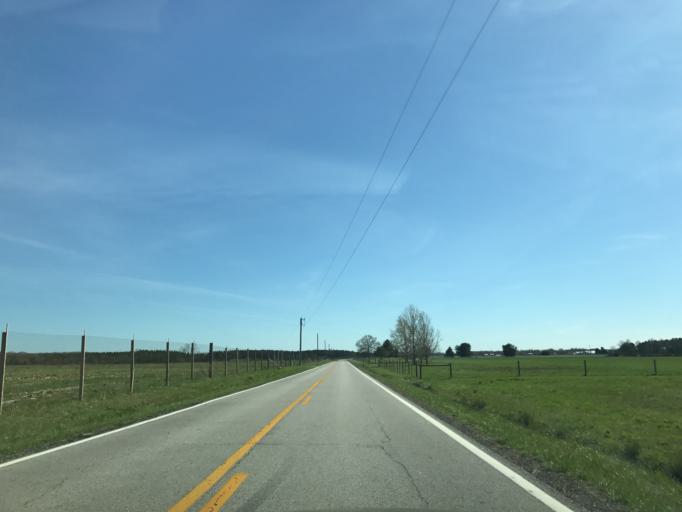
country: US
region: Maryland
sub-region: Caroline County
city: Ridgely
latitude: 38.9542
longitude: -75.9783
